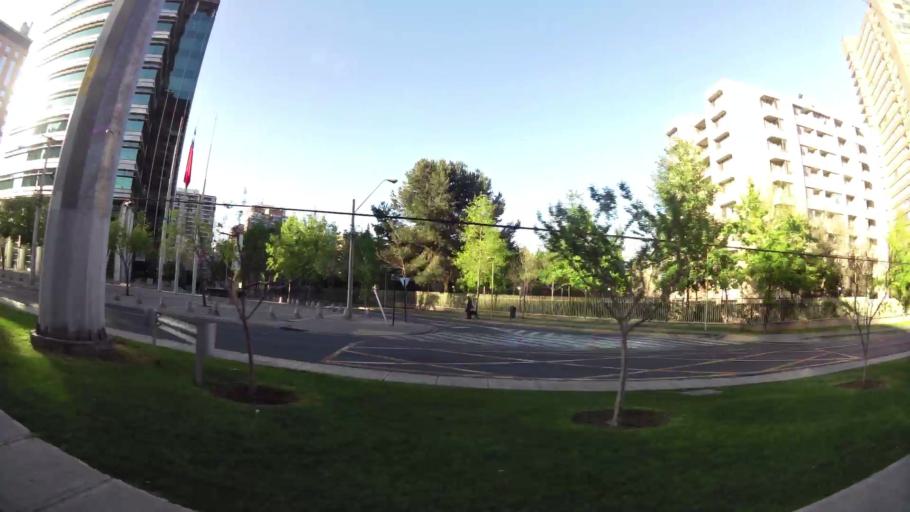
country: CL
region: Santiago Metropolitan
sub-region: Provincia de Santiago
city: Villa Presidente Frei, Nunoa, Santiago, Chile
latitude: -33.4063
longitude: -70.5775
